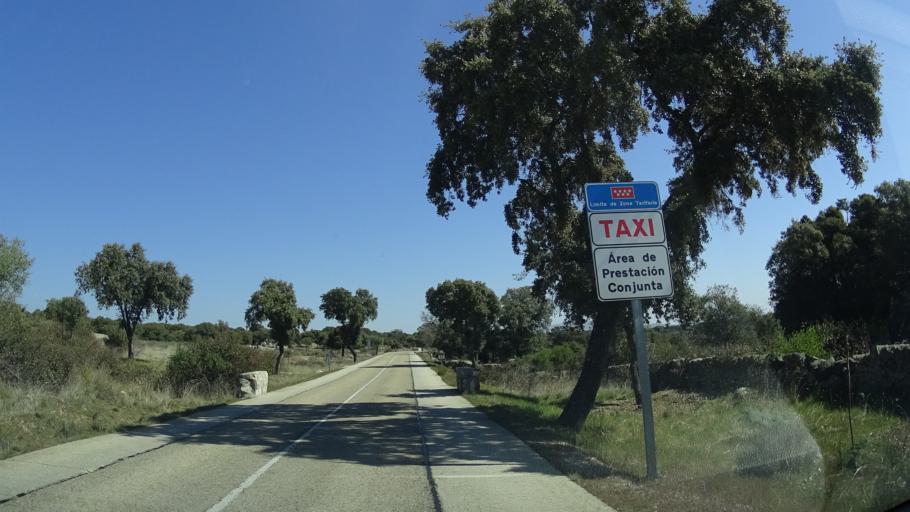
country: ES
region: Madrid
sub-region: Provincia de Madrid
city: Hoyo de Manzanares
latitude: 40.6417
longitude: -3.8469
